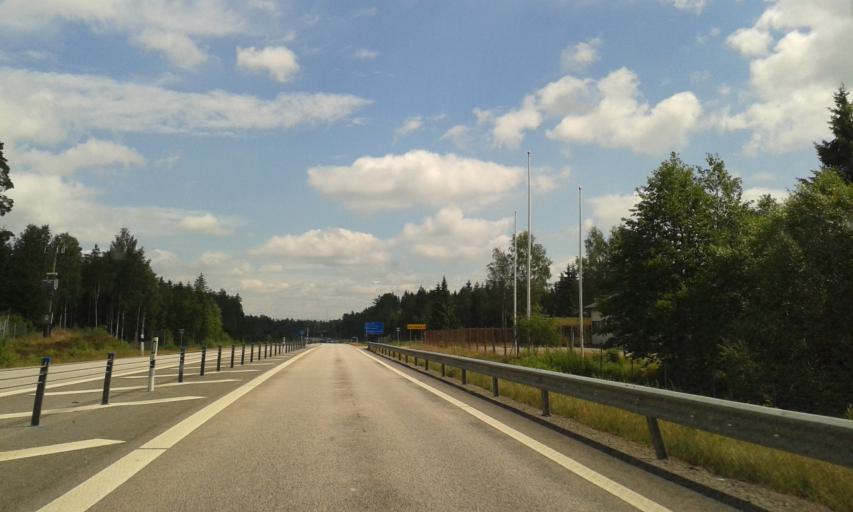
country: SE
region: Kronoberg
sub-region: Alvesta Kommun
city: Alvesta
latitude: 56.9148
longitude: 14.4890
